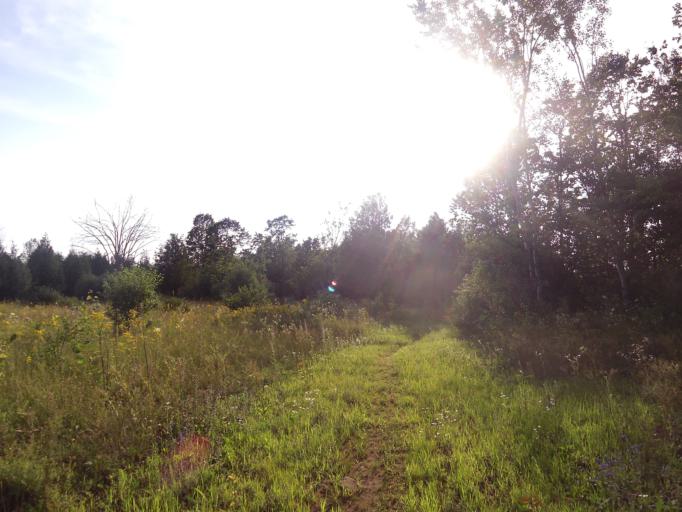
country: CA
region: Ontario
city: Bells Corners
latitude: 45.3144
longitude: -75.8716
